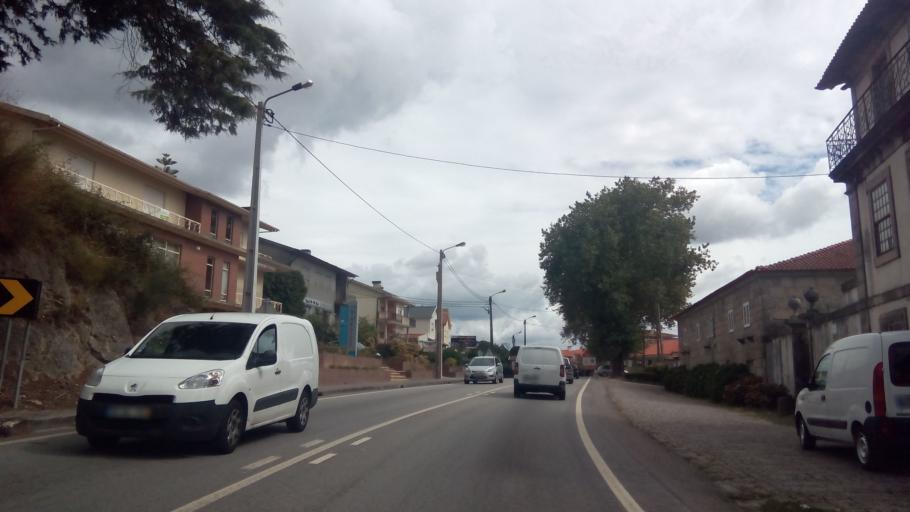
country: PT
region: Porto
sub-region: Paredes
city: Baltar
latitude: 41.1910
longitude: -8.4013
